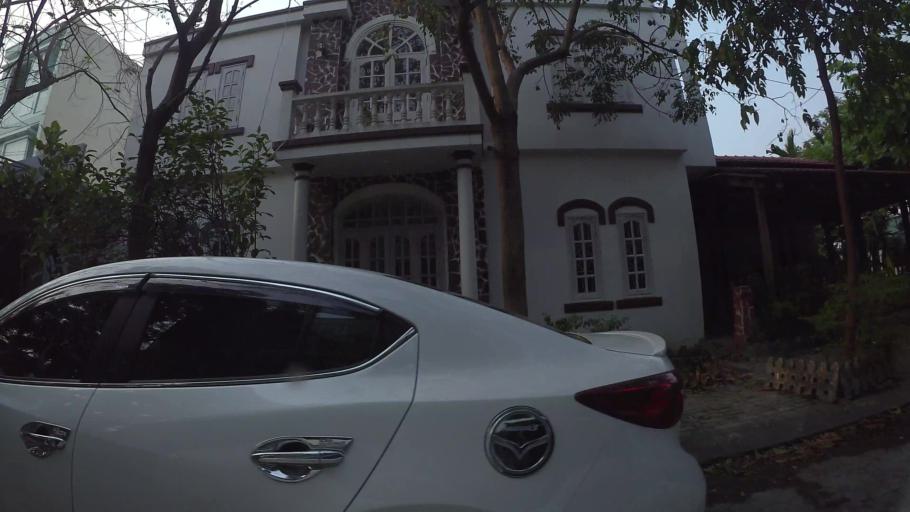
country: VN
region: Da Nang
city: Cam Le
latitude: 16.0219
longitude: 108.1984
